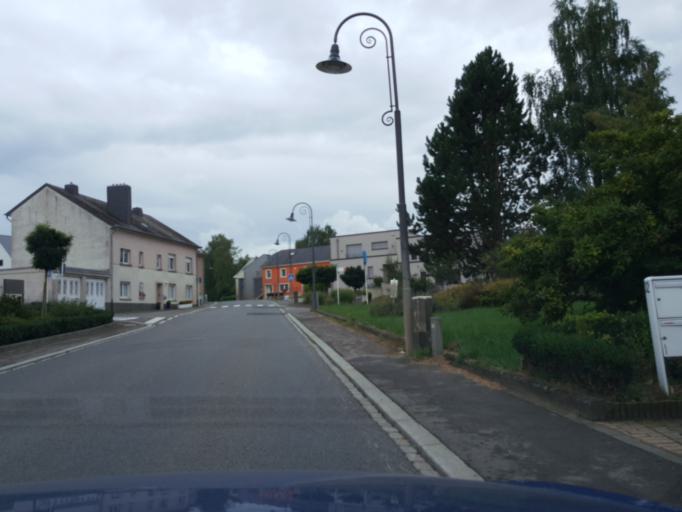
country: LU
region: Luxembourg
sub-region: Canton de Capellen
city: Kehlen
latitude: 49.6652
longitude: 6.0349
